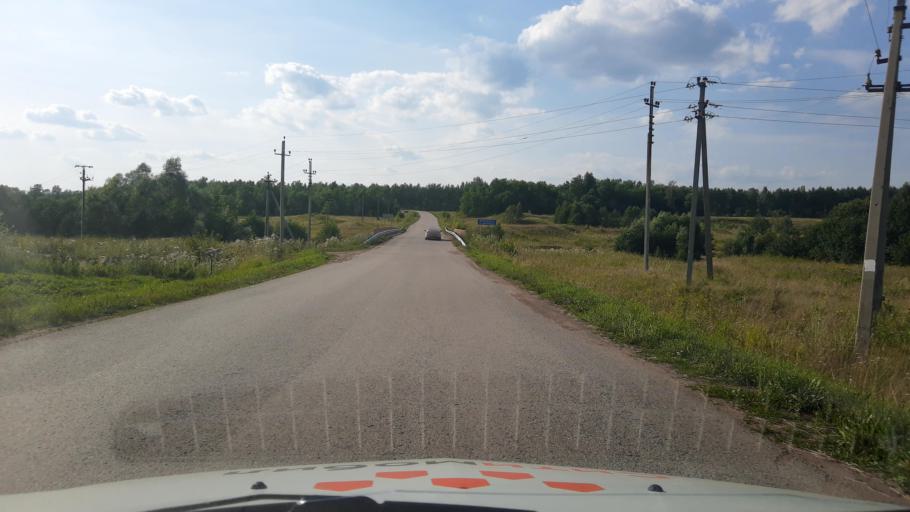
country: RU
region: Bashkortostan
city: Kabakovo
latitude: 54.6609
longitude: 56.2008
